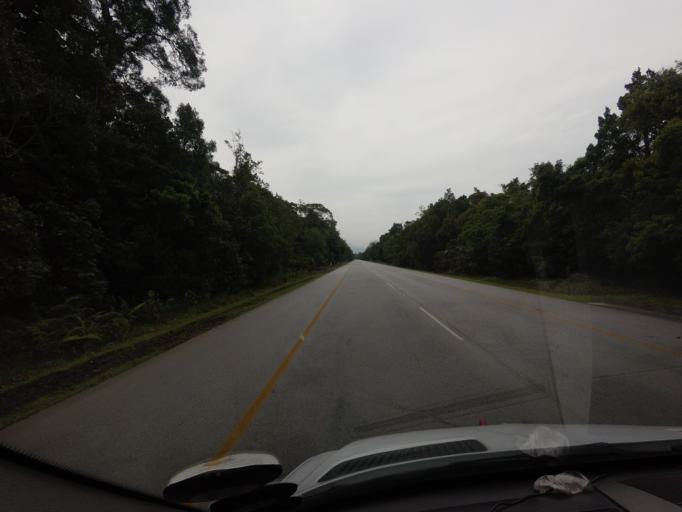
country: ZA
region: Eastern Cape
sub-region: Cacadu District Municipality
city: Kareedouw
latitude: -33.9703
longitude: 23.8475
